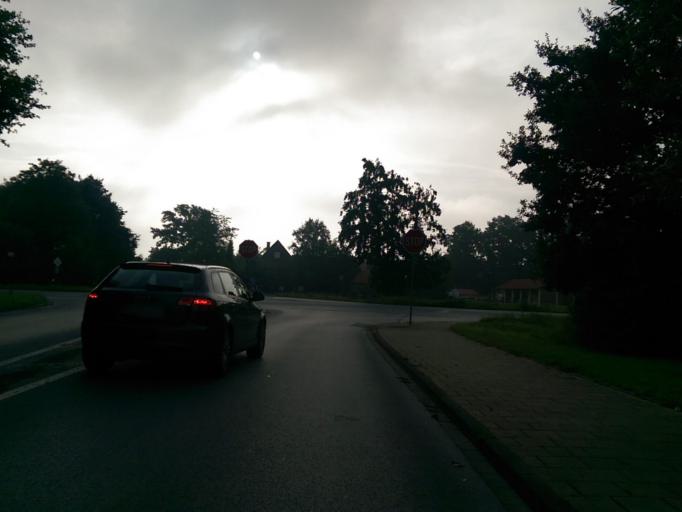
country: DE
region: North Rhine-Westphalia
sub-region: Regierungsbezirk Detmold
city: Harsewinkel
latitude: 51.9580
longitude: 8.2512
